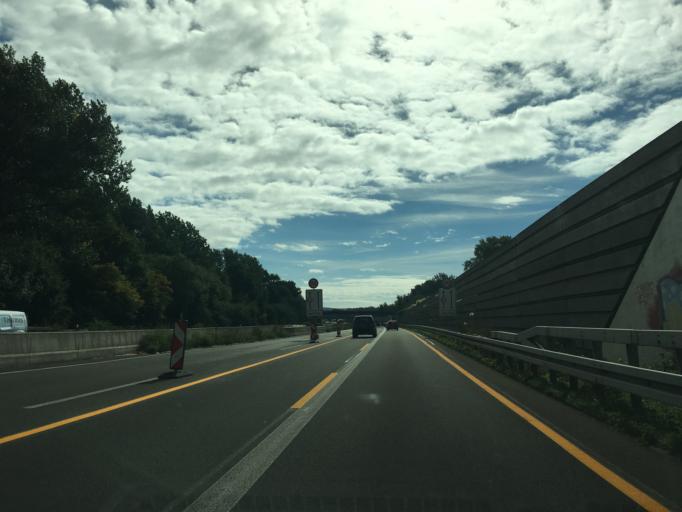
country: DE
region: North Rhine-Westphalia
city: Loehne
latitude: 52.2050
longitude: 8.7311
